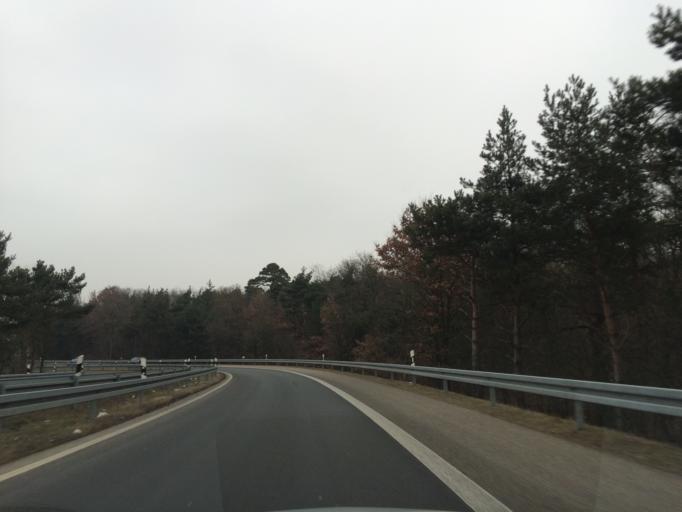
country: DE
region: Hesse
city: Morfelden-Walldorf
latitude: 50.0349
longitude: 8.5976
